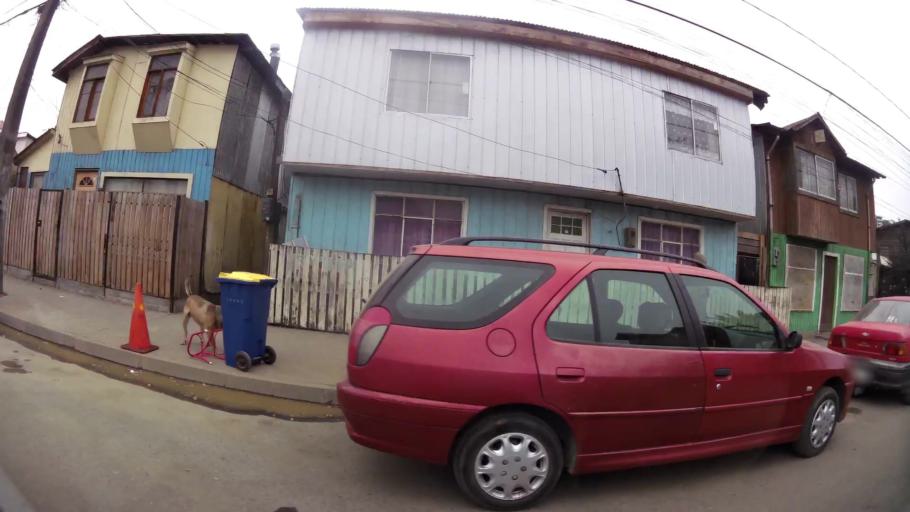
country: CL
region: Biobio
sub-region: Provincia de Concepcion
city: Concepcion
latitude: -36.8397
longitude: -73.0580
